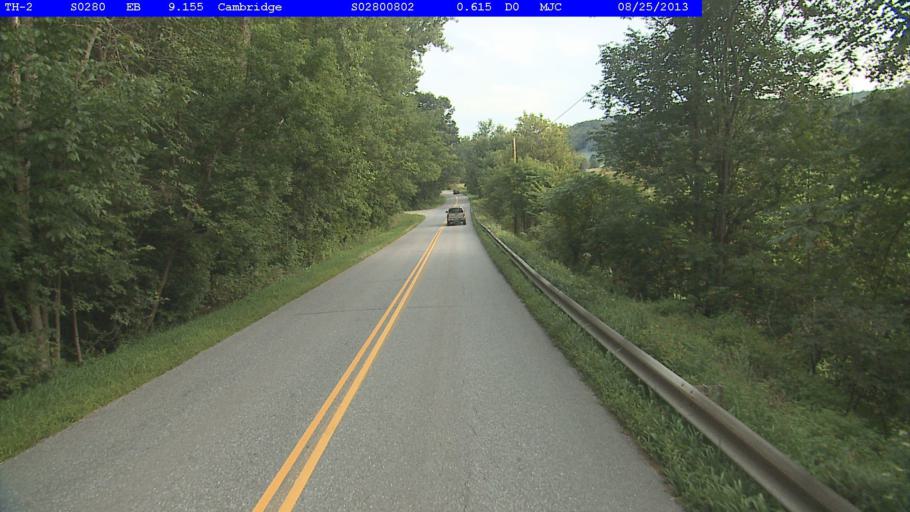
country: US
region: Vermont
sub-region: Chittenden County
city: Jericho
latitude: 44.6546
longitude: -72.8806
